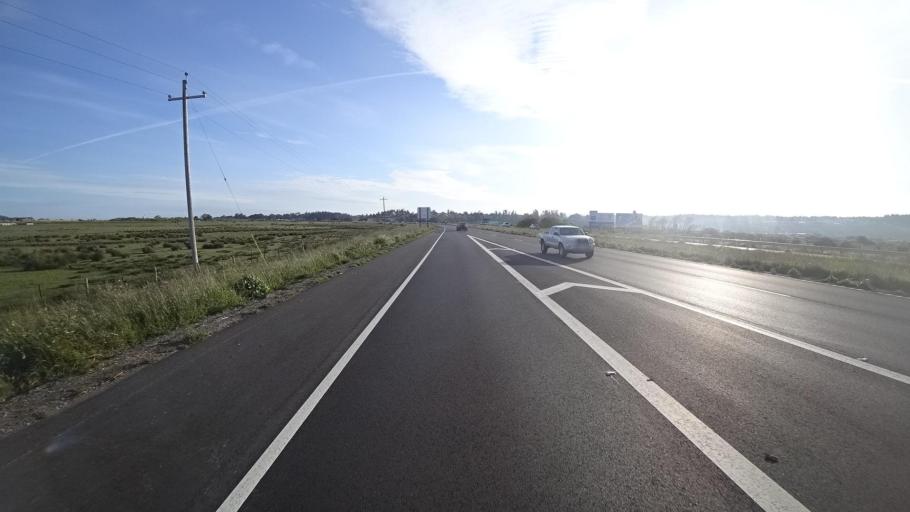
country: US
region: California
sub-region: Humboldt County
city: Humboldt Hill
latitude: 40.7485
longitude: -124.1966
